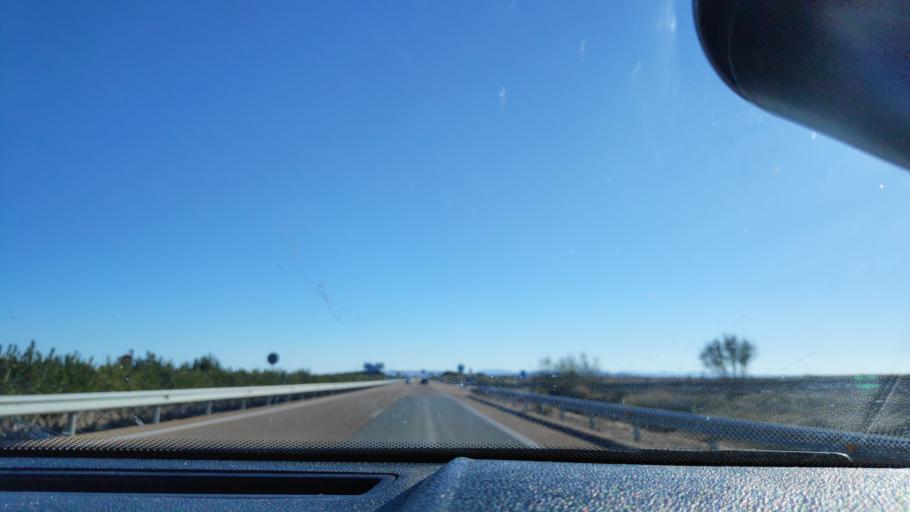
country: ES
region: Extremadura
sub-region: Provincia de Badajoz
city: Los Santos de Maimona
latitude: 38.4183
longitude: -6.3449
